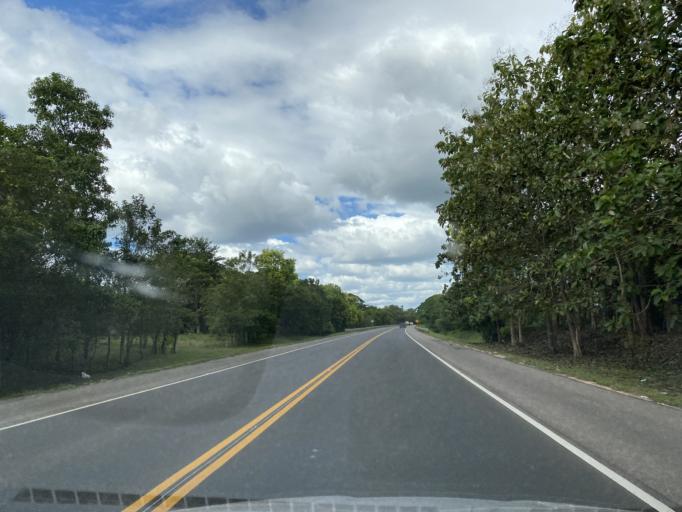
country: DO
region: Santo Domingo
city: Guerra
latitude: 18.5986
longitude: -69.7710
